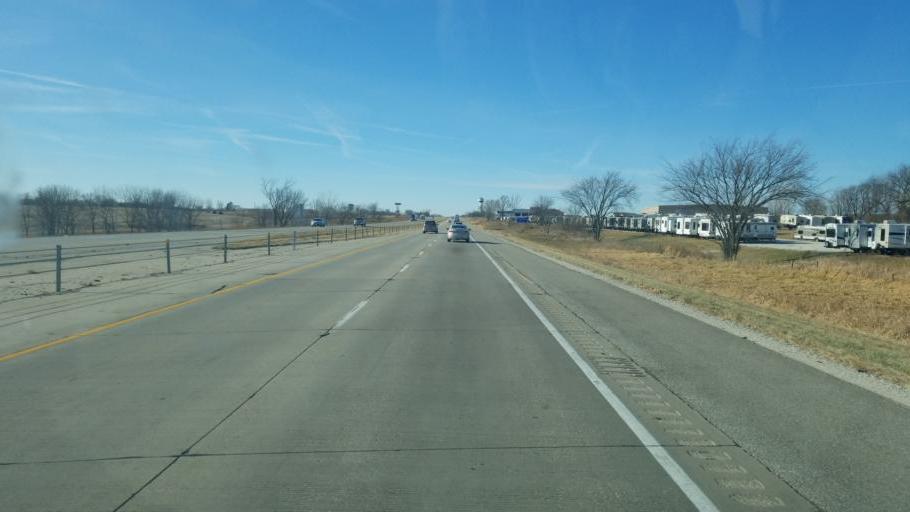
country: US
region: Iowa
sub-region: Dallas County
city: De Soto
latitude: 41.5421
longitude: -93.9968
